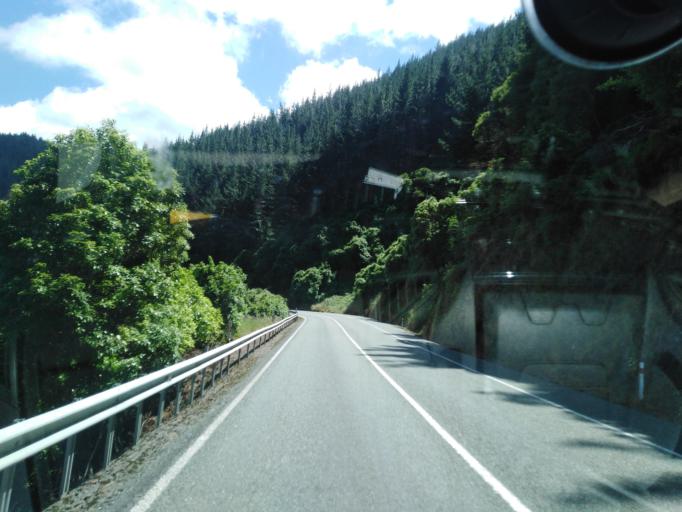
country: NZ
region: Nelson
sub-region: Nelson City
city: Nelson
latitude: -41.2291
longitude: 173.4121
